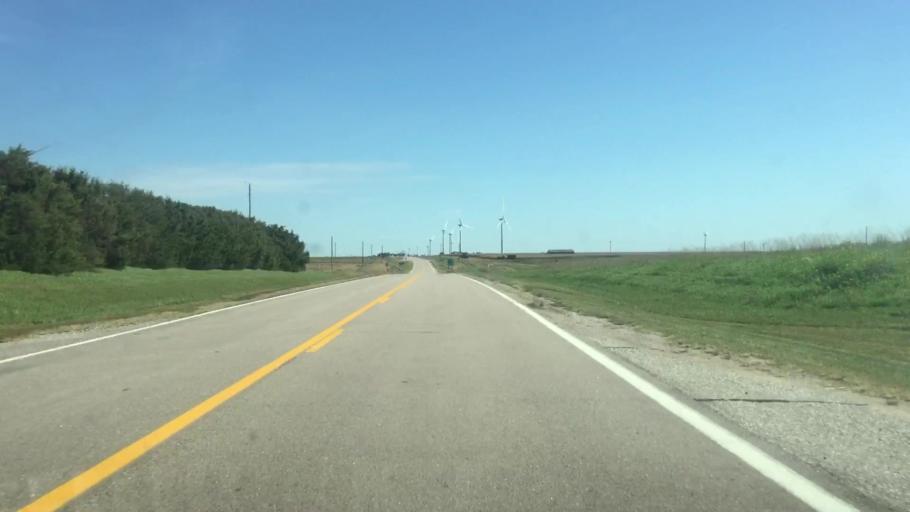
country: US
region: Kansas
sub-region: Washington County
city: Washington
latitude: 40.0450
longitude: -96.9410
